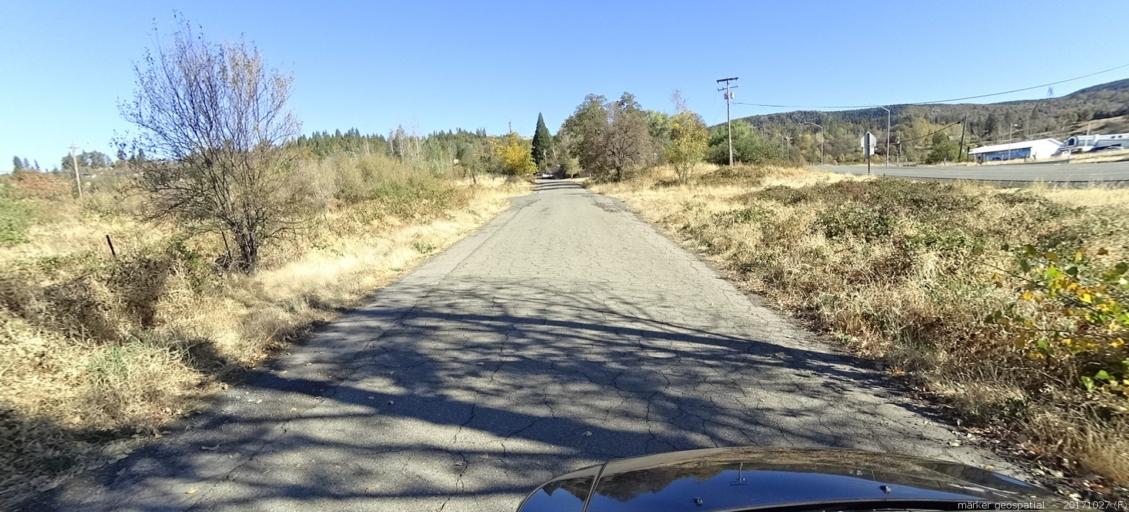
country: US
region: California
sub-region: Shasta County
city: Burney
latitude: 40.8428
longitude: -121.9233
